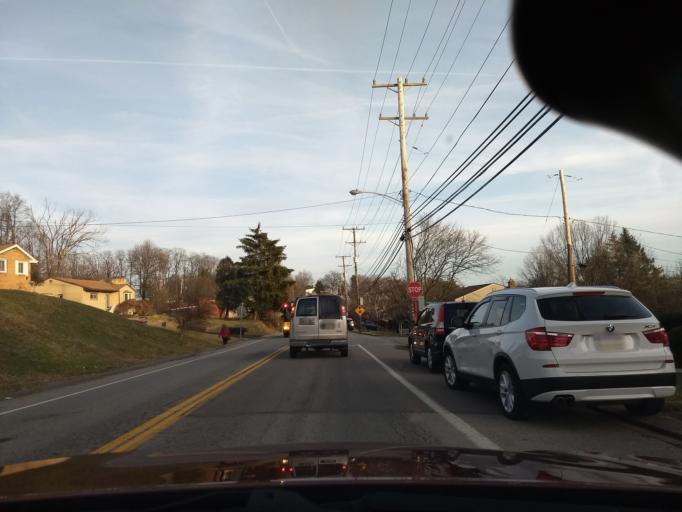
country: US
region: Pennsylvania
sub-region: Allegheny County
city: Brentwood
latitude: 40.3633
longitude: -79.9670
